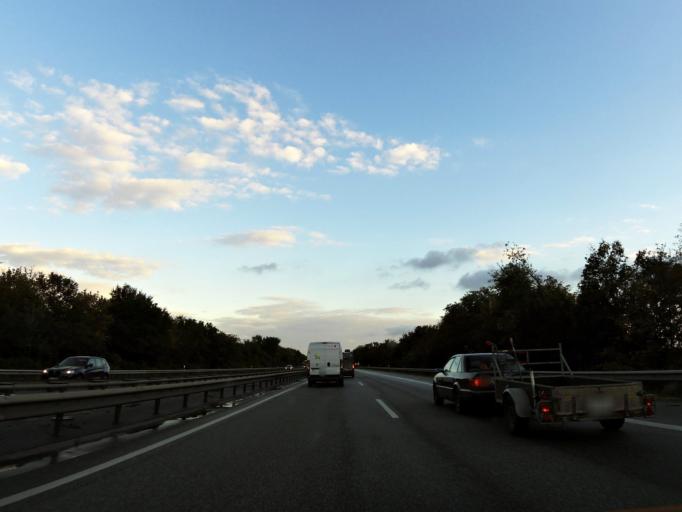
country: DE
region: Rheinland-Pfalz
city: Welgesheim
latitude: 49.8824
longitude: 7.9490
